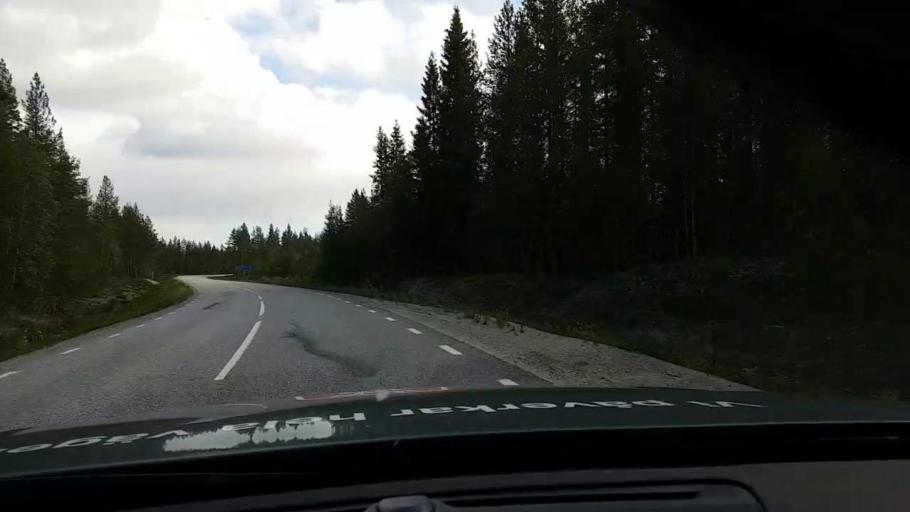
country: SE
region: Vaesternorrland
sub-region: OErnskoeldsviks Kommun
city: Bredbyn
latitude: 63.6860
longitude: 17.7723
